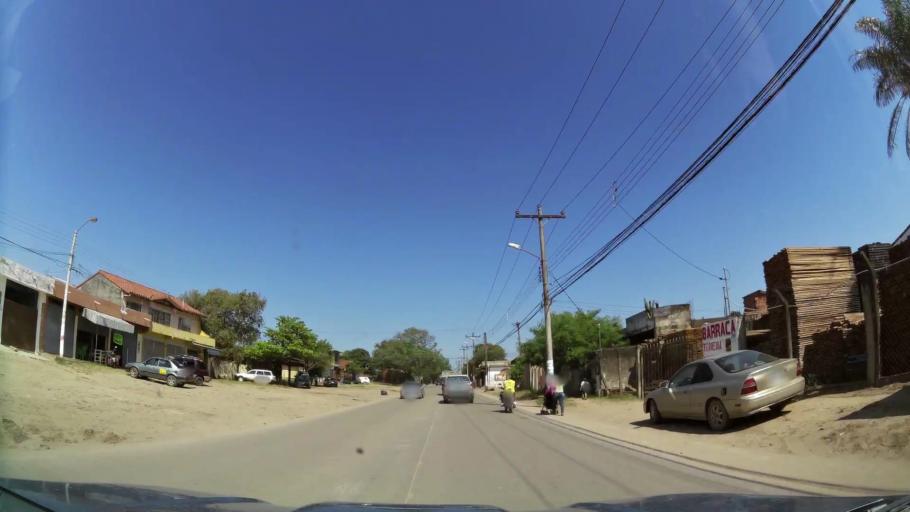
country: BO
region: Santa Cruz
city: Santa Cruz de la Sierra
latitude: -17.7500
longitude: -63.1218
